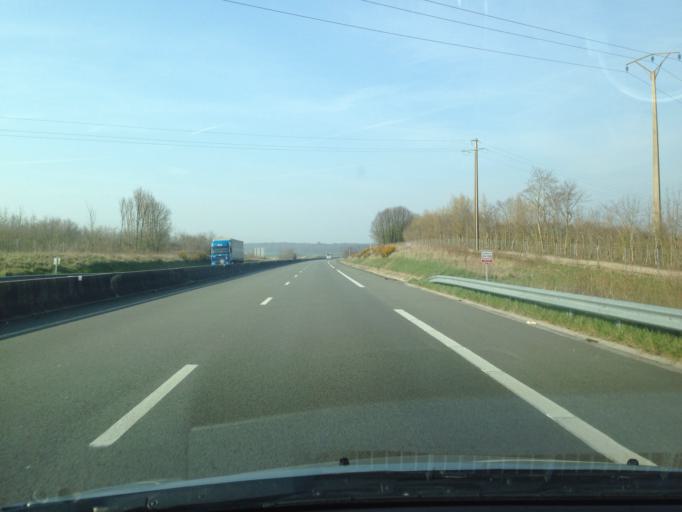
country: FR
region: Nord-Pas-de-Calais
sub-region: Departement du Pas-de-Calais
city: Saint-Josse
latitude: 50.4376
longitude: 1.6932
